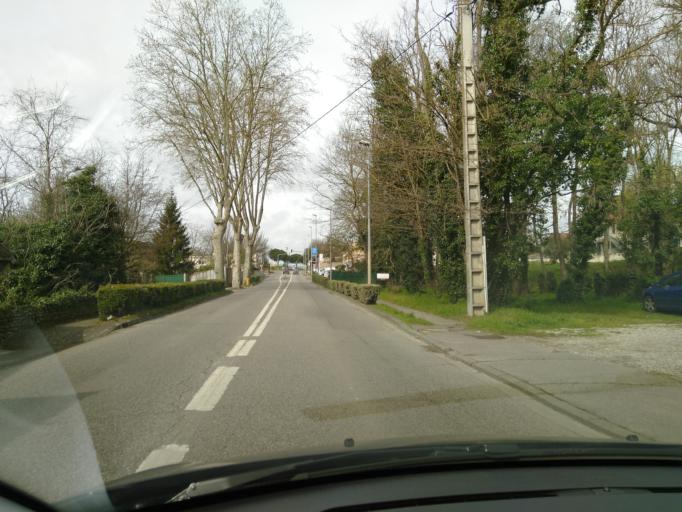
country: FR
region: Midi-Pyrenees
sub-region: Departement de la Haute-Garonne
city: Seilh
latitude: 43.6941
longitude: 1.3528
